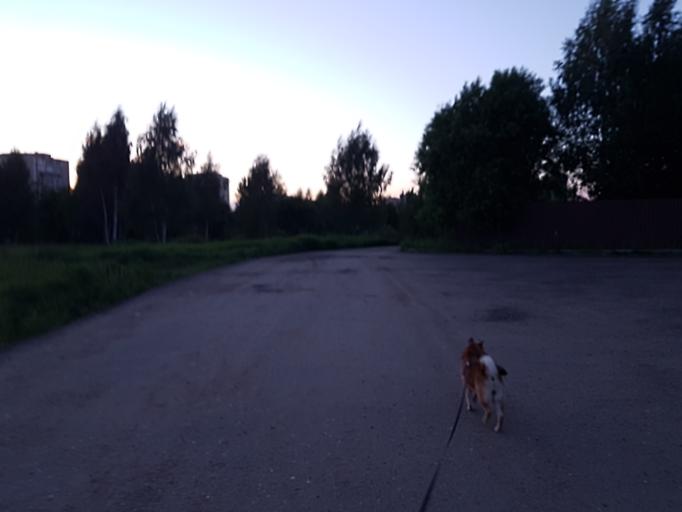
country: RU
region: Moskovskaya
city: Istra
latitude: 55.9063
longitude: 36.8773
